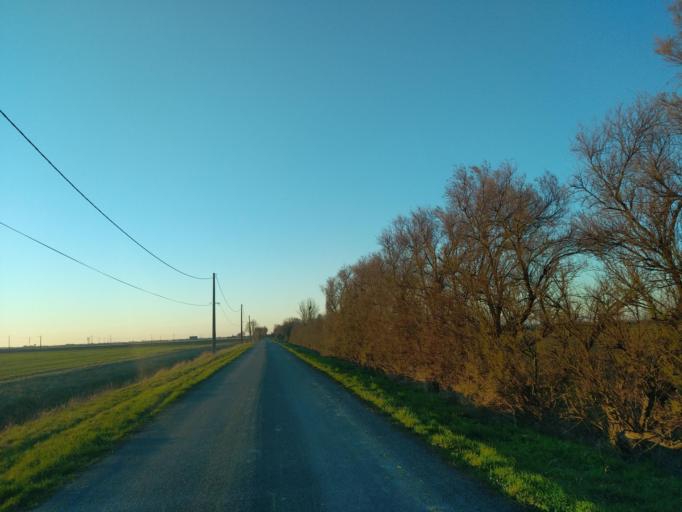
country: FR
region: Pays de la Loire
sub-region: Departement de la Vendee
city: Triaize
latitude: 46.3745
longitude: -1.3010
